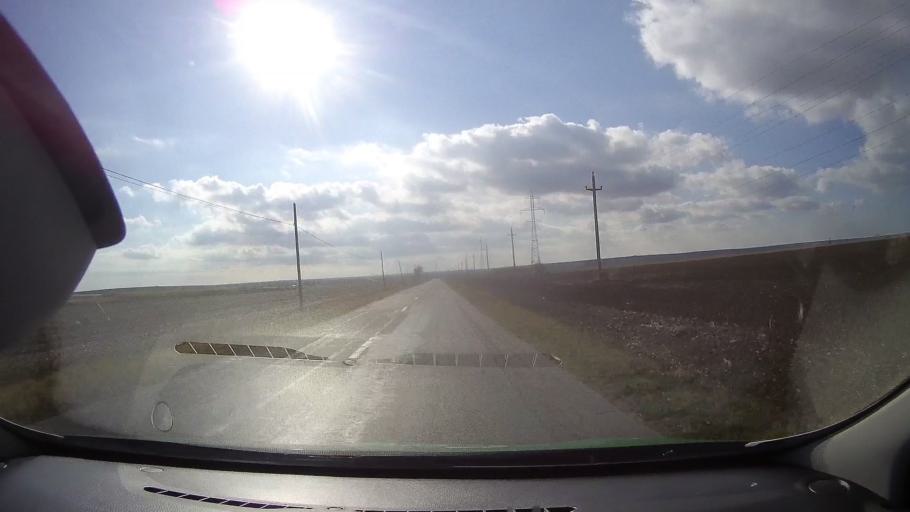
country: RO
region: Constanta
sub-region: Comuna Istria
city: Istria
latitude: 44.5389
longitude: 28.6885
